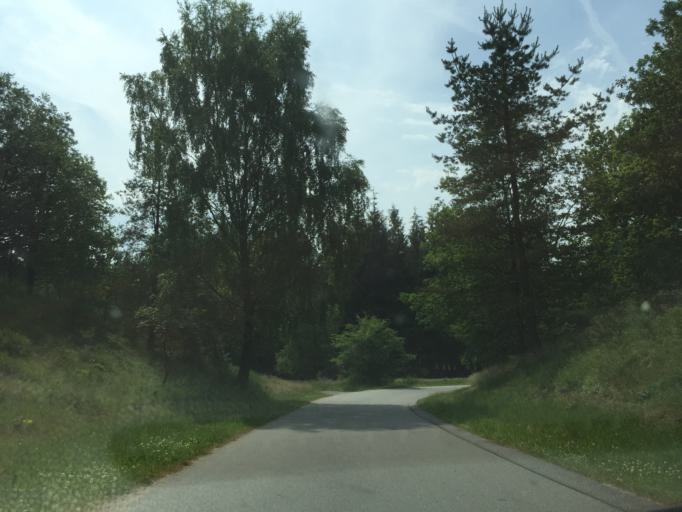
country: DK
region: Central Jutland
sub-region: Silkeborg Kommune
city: Virklund
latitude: 56.0649
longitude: 9.4689
